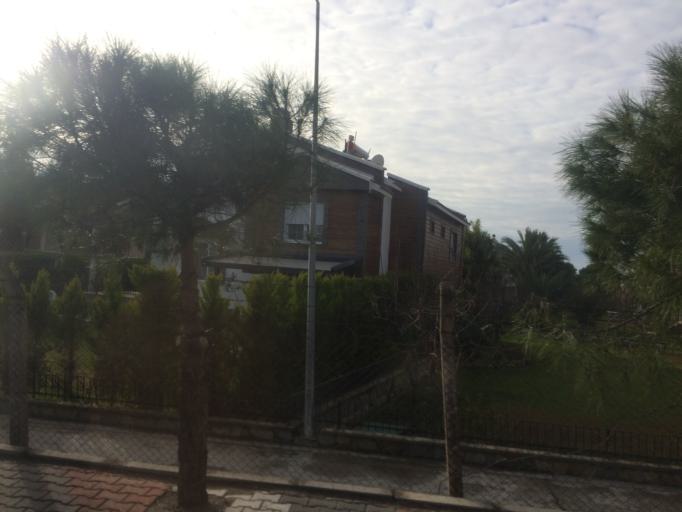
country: TR
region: Izmir
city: Menemen
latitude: 38.5051
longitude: 26.9587
